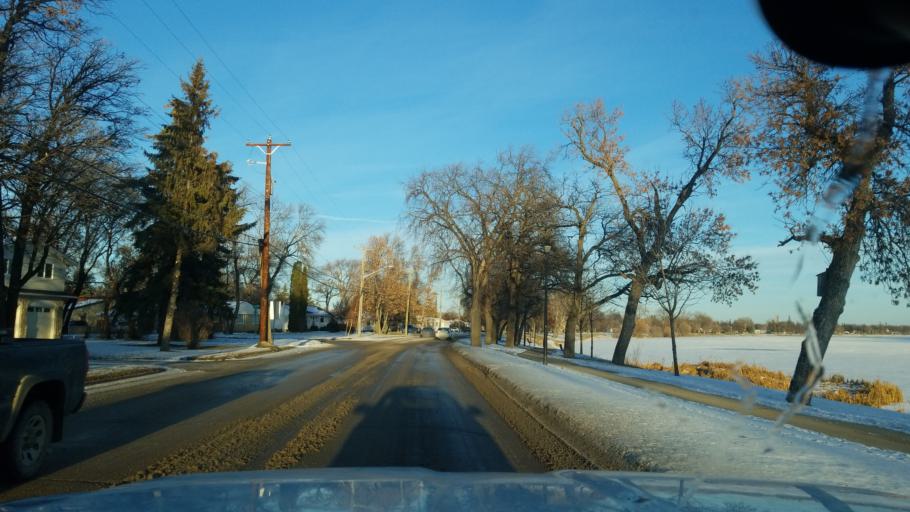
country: CA
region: Manitoba
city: Portage la Prairie
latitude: 49.9682
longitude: -98.3158
